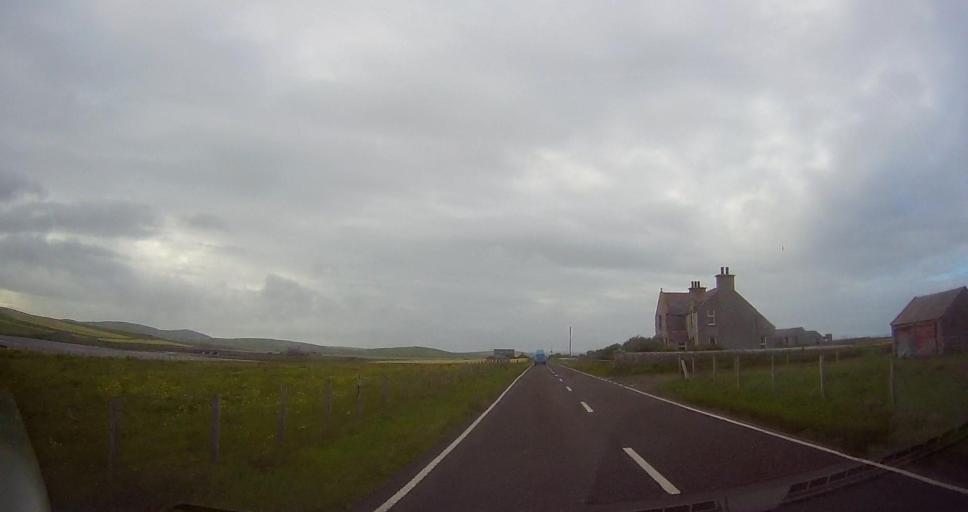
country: GB
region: Scotland
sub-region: Orkney Islands
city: Stromness
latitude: 58.9796
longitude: -3.2440
